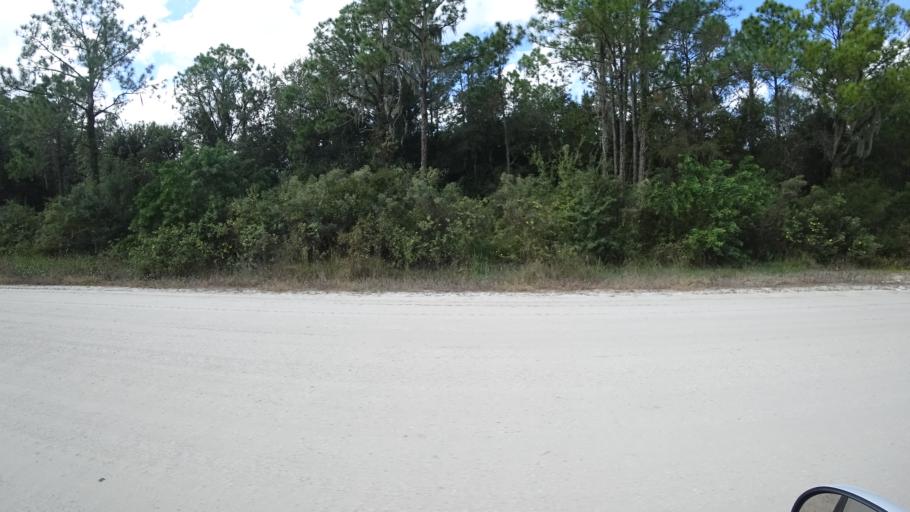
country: US
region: Florida
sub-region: Hillsborough County
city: Wimauma
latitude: 27.4538
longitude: -82.1840
